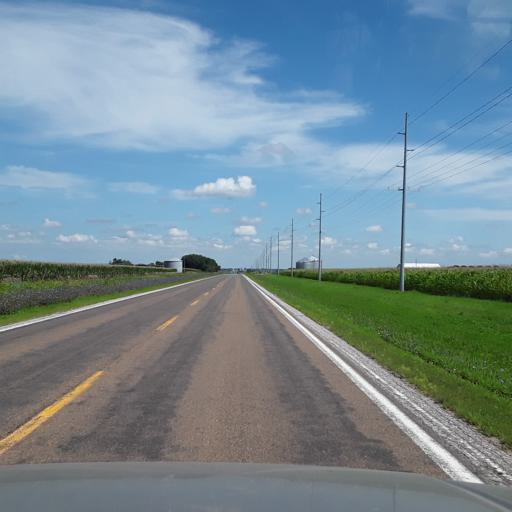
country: US
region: Nebraska
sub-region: York County
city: York
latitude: 40.9563
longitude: -97.4061
